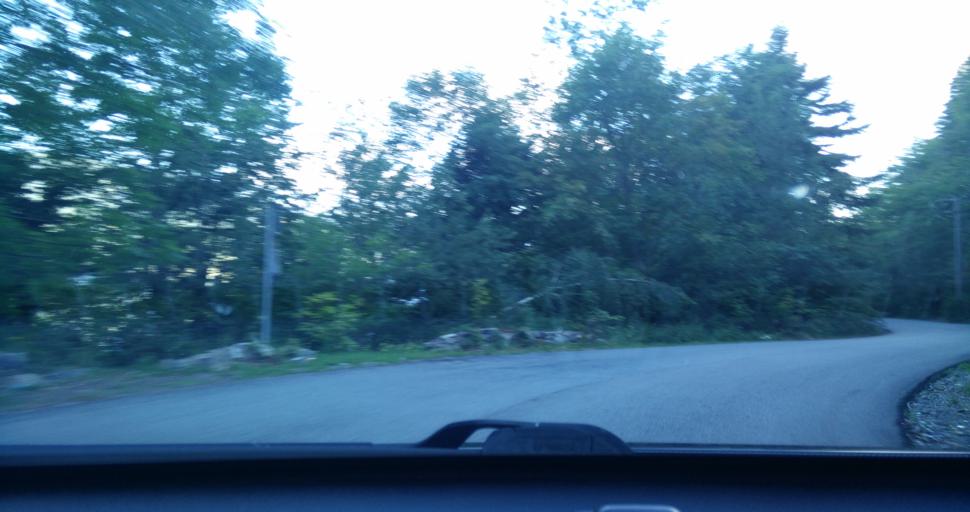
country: RO
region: Bihor
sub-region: Oras Nucet
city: Nucet
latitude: 46.5149
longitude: 22.6344
